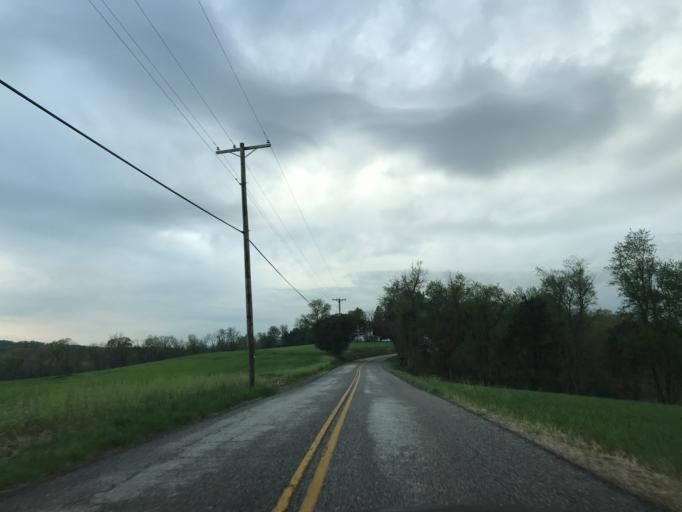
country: US
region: Maryland
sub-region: Harford County
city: Jarrettsville
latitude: 39.6705
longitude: -76.4600
